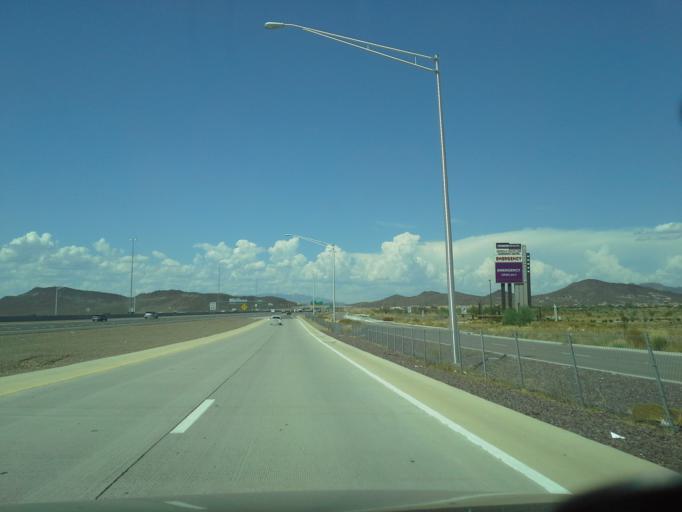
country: US
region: Arizona
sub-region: Maricopa County
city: Anthem
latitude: 33.7859
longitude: -112.1322
